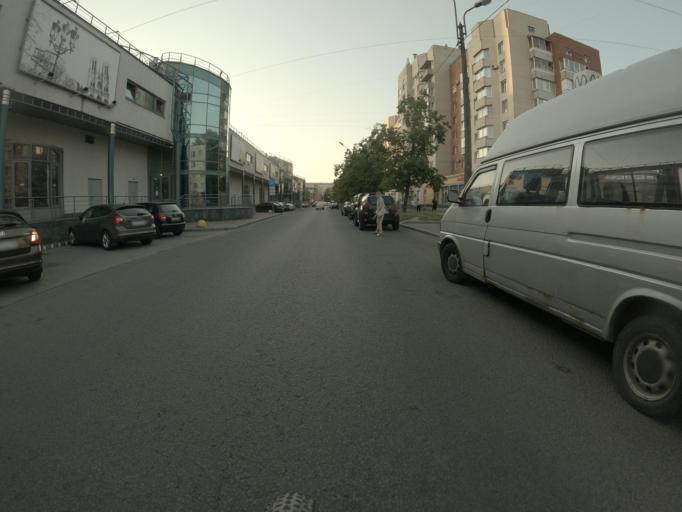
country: RU
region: St.-Petersburg
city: Dachnoye
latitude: 59.8498
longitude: 30.2689
